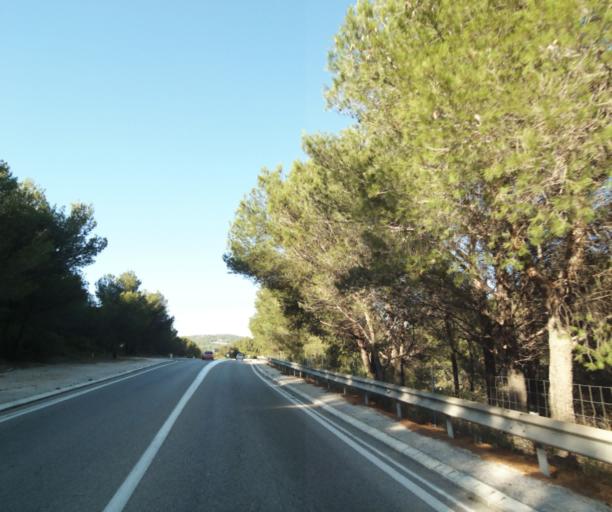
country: FR
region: Provence-Alpes-Cote d'Azur
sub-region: Departement des Bouches-du-Rhone
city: Roquefort-la-Bedoule
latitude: 43.2206
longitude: 5.5803
